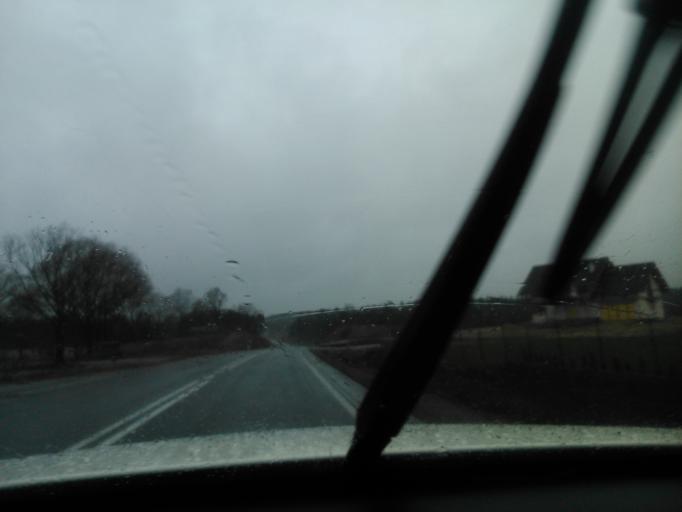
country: PL
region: Kujawsko-Pomorskie
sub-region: Powiat golubsko-dobrzynski
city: Radomin
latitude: 53.1008
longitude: 19.1356
